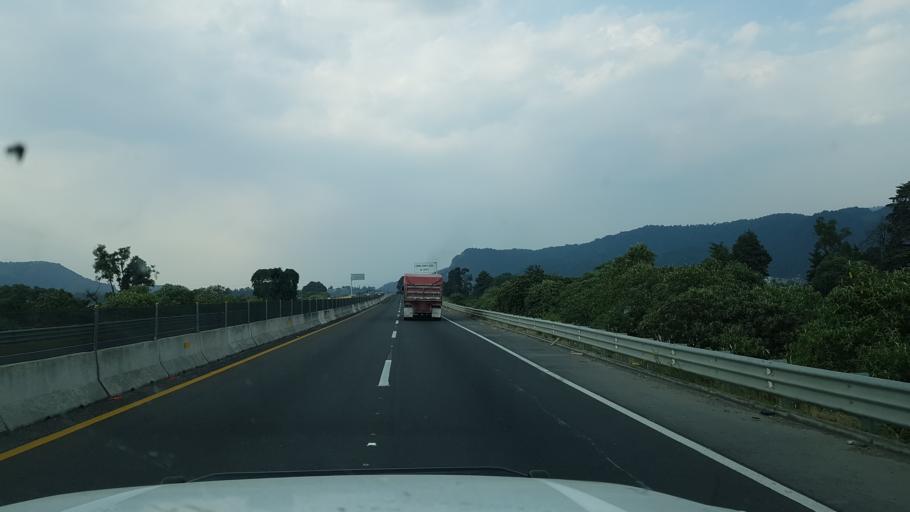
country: MX
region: Mexico
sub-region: Ayapango
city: La Colonia
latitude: 19.1421
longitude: -98.7760
